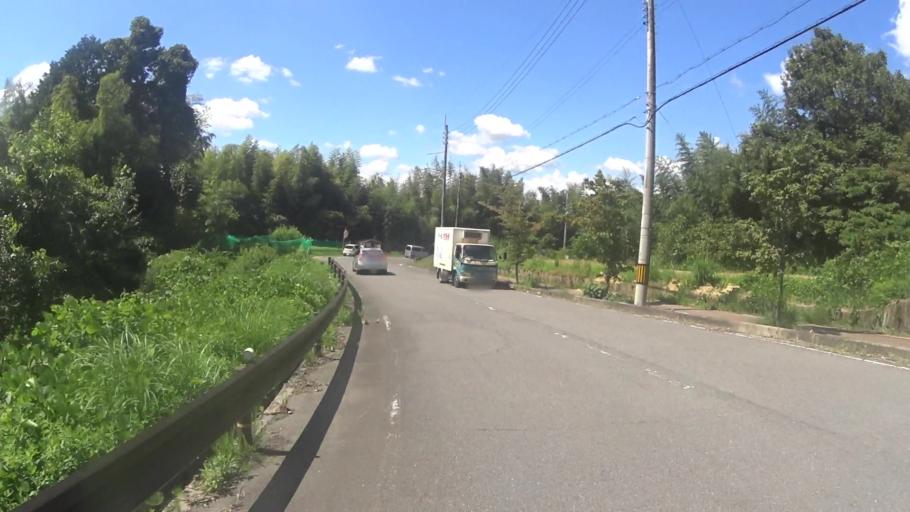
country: JP
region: Nara
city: Nara-shi
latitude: 34.7201
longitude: 135.8678
